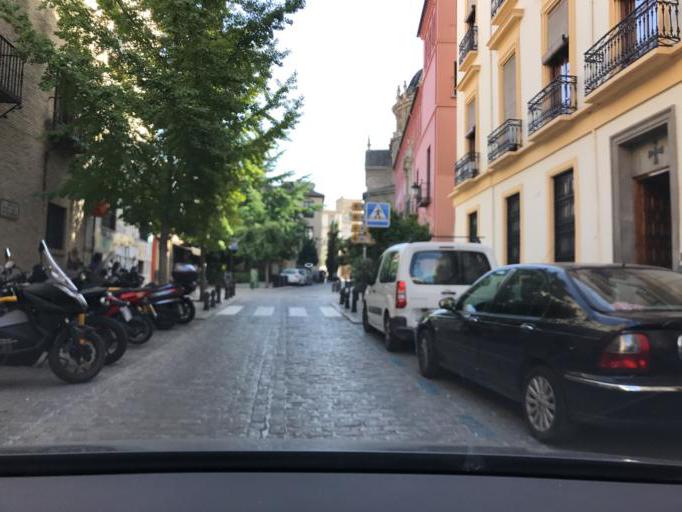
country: ES
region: Andalusia
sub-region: Provincia de Granada
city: Granada
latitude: 37.1794
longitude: -3.6021
